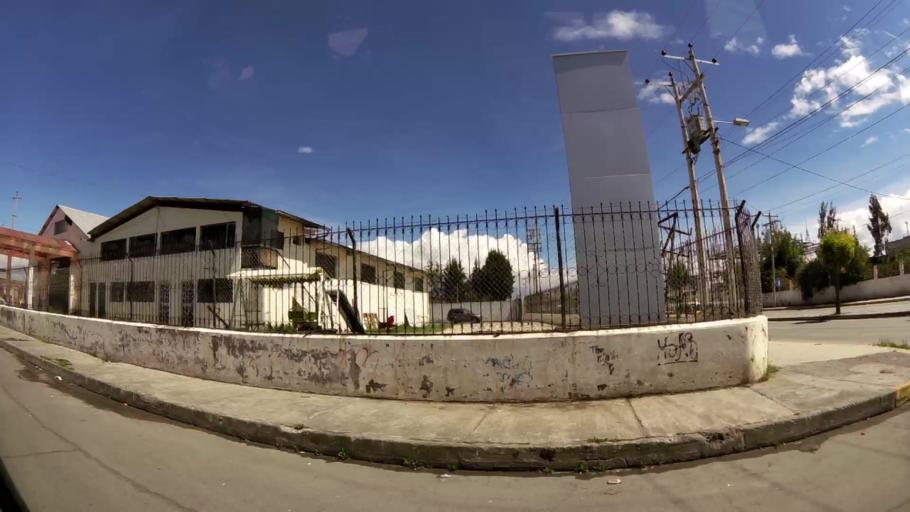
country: EC
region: Chimborazo
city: Riobamba
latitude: -1.6821
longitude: -78.6302
